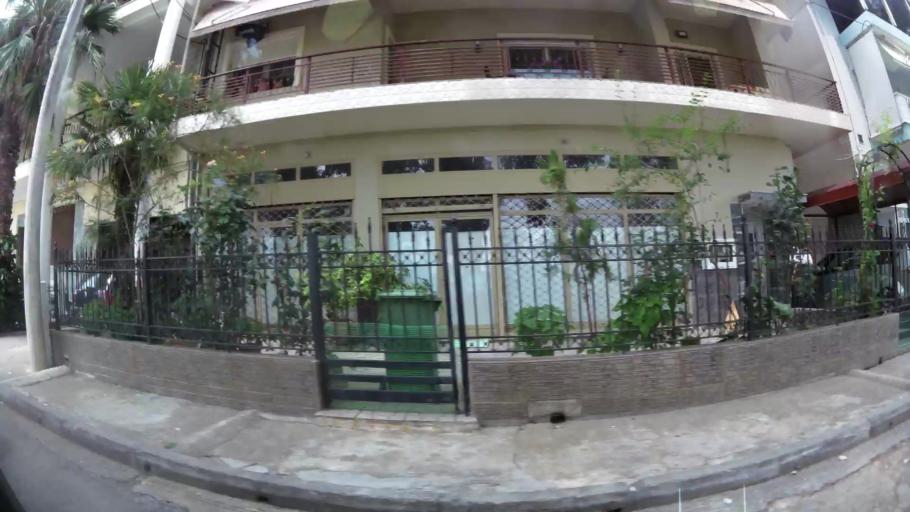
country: GR
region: Central Macedonia
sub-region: Nomos Pierias
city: Kallithea
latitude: 40.2714
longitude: 22.5764
